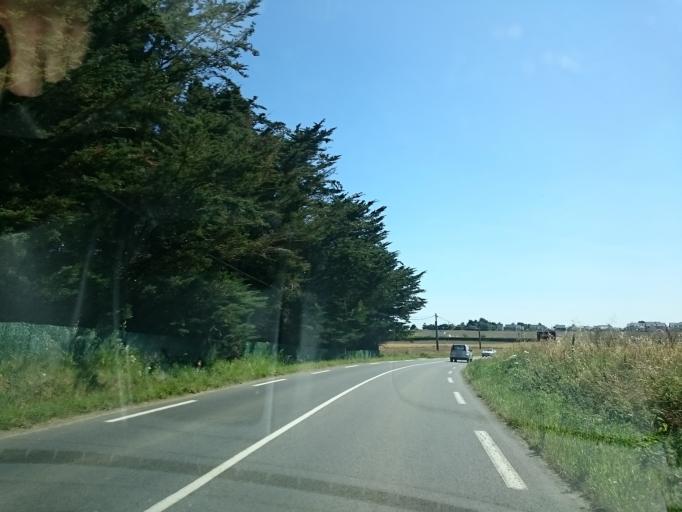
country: FR
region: Brittany
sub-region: Departement d'Ille-et-Vilaine
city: Saint-Coulomb
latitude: 48.6645
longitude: -1.9585
